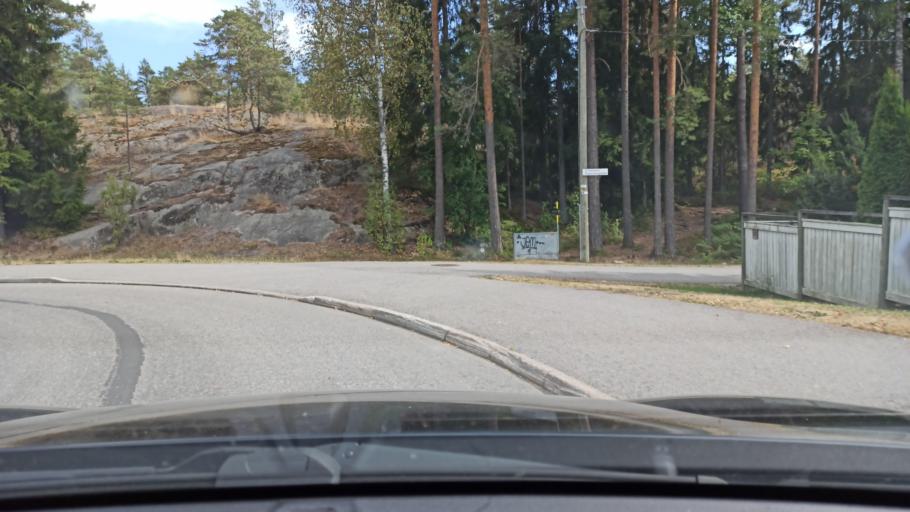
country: FI
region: Uusimaa
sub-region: Helsinki
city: Espoo
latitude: 60.1613
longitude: 24.6544
